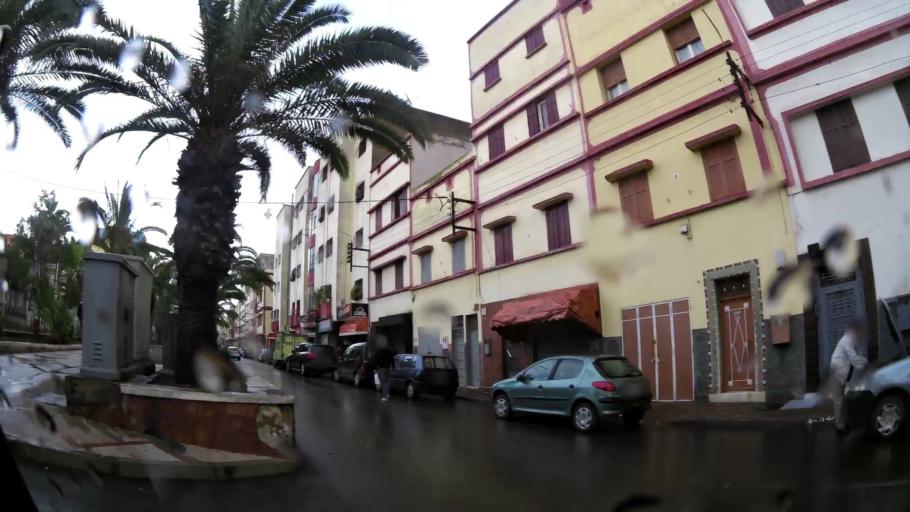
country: MA
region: Grand Casablanca
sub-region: Casablanca
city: Casablanca
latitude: 33.5487
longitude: -7.5833
